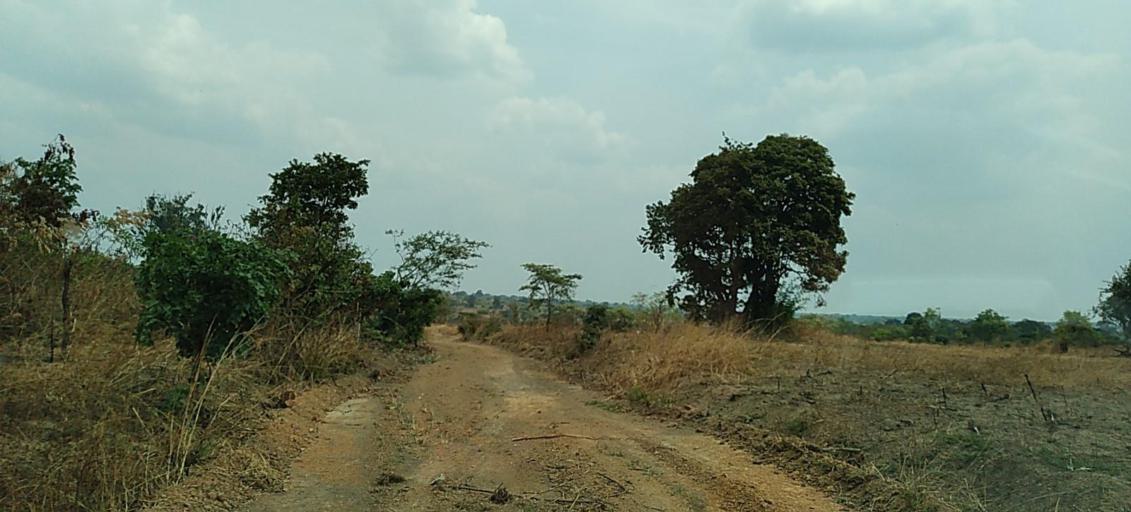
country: ZM
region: Copperbelt
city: Chililabombwe
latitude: -12.3593
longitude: 27.8004
